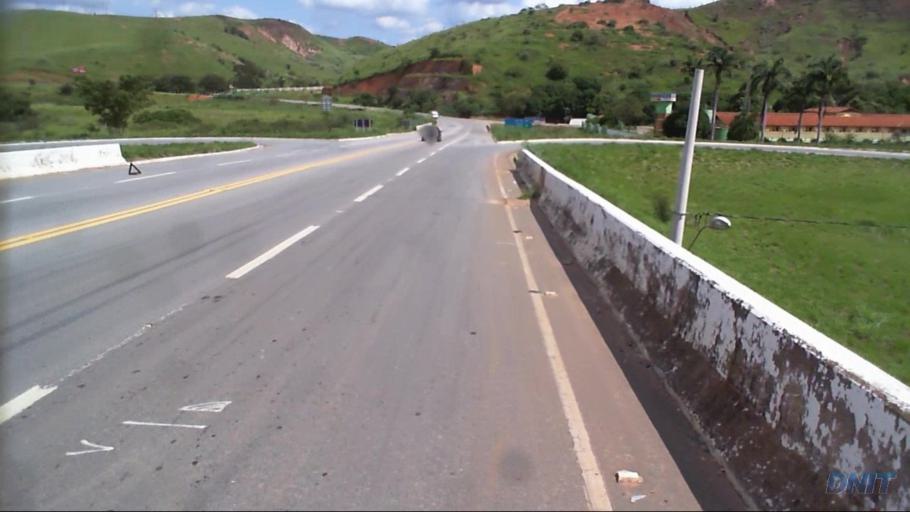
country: BR
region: Minas Gerais
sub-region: Governador Valadares
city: Governador Valadares
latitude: -18.8460
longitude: -41.9806
